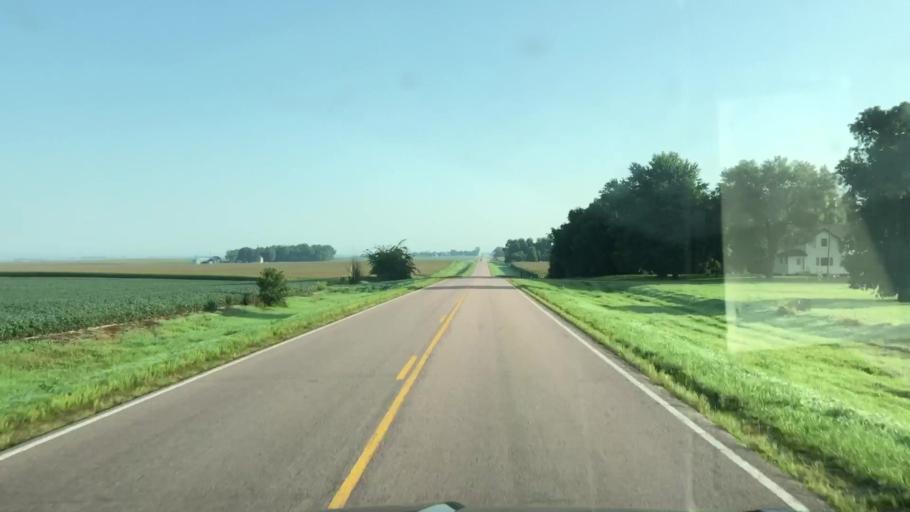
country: US
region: Iowa
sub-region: Lyon County
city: George
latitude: 43.2927
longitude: -95.9995
